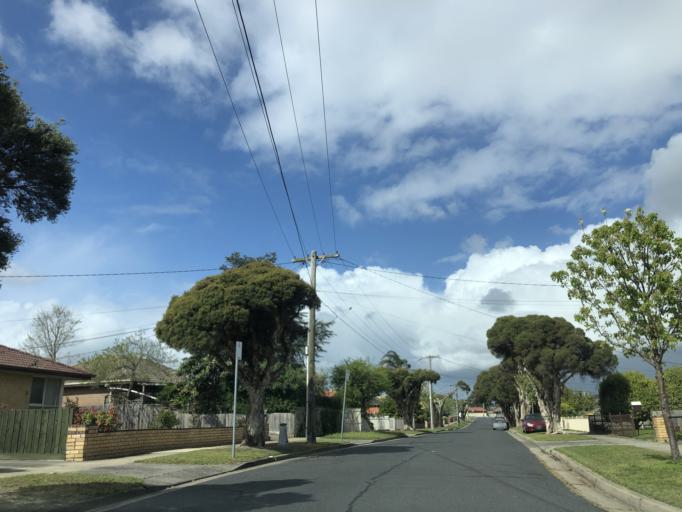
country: AU
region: Victoria
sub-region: Kingston
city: Clayton South
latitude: -37.9348
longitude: 145.1154
